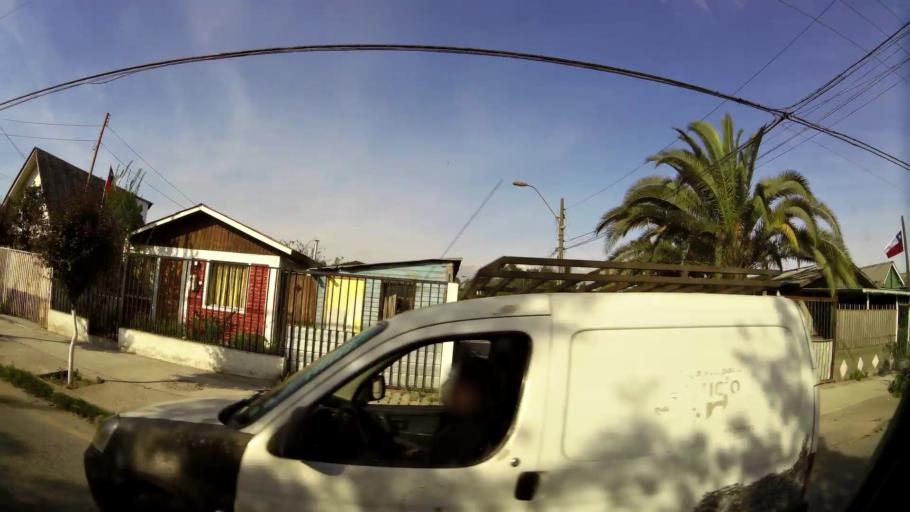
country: CL
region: Santiago Metropolitan
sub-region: Provincia de Santiago
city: Santiago
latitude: -33.5114
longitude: -70.6317
